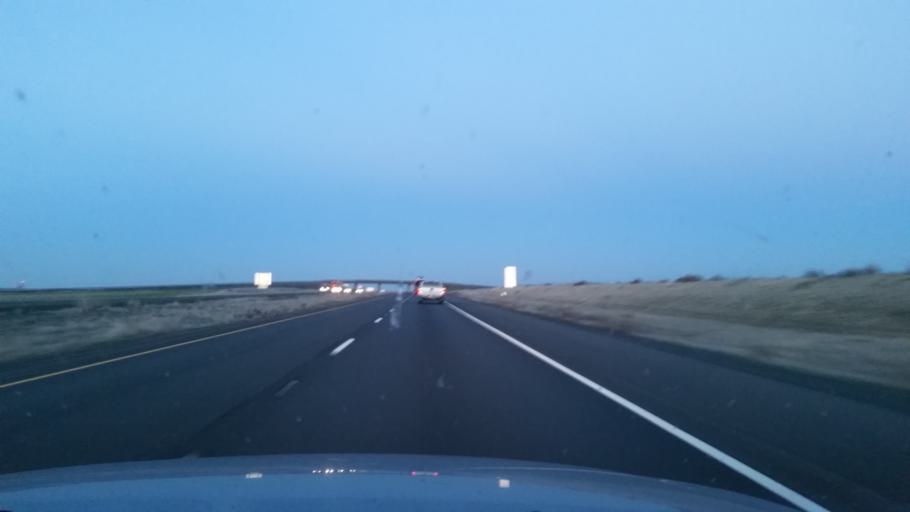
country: US
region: Washington
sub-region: Adams County
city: Ritzville
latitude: 47.1222
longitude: -118.3574
